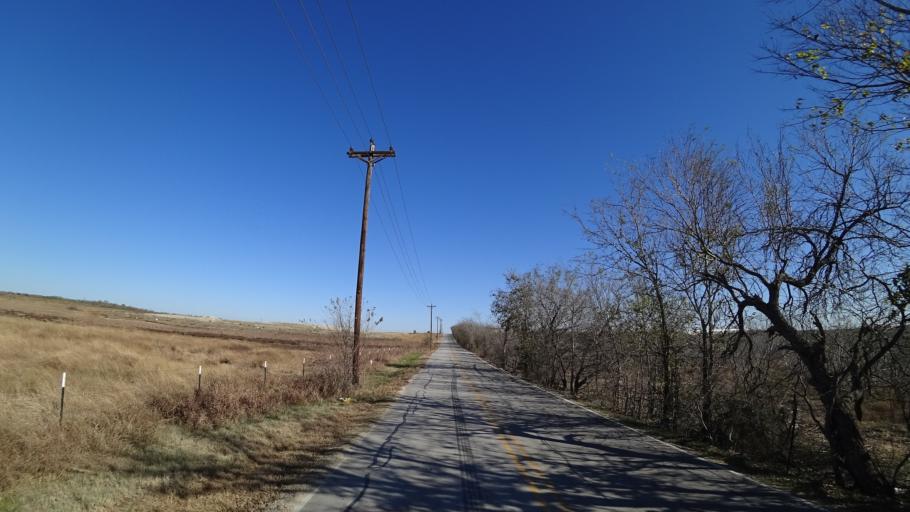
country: US
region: Texas
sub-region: Travis County
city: Onion Creek
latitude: 30.1157
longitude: -97.6716
